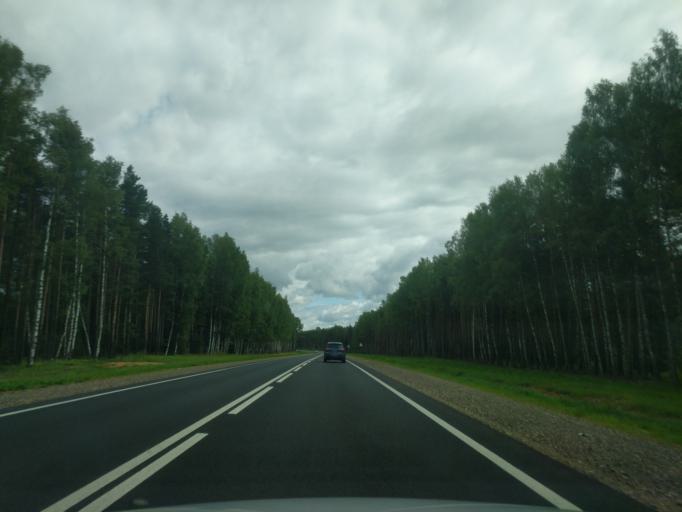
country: RU
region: Jaroslavl
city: Tunoshna
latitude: 57.5630
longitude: 40.2456
